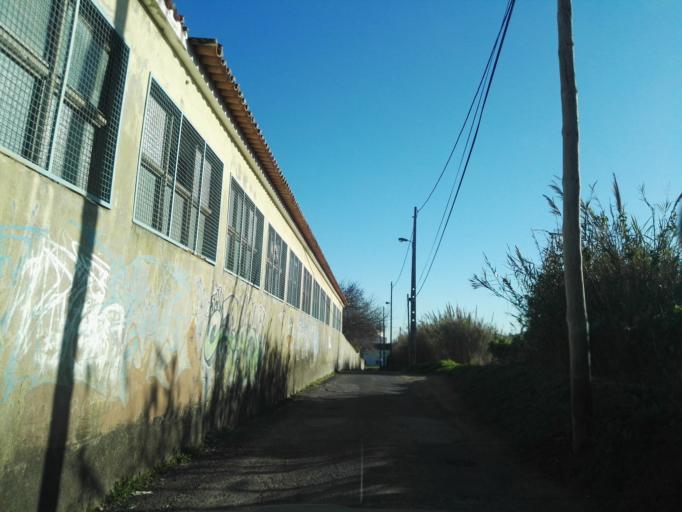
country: PT
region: Lisbon
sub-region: Odivelas
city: Pontinha
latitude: 38.7628
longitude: -9.1856
